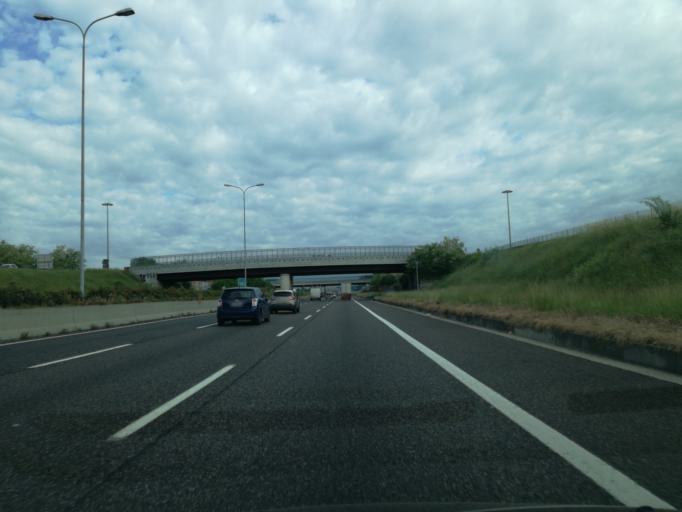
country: IT
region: Lombardy
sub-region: Provincia di Monza e Brianza
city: Carate Brianza
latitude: 45.6640
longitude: 9.2234
